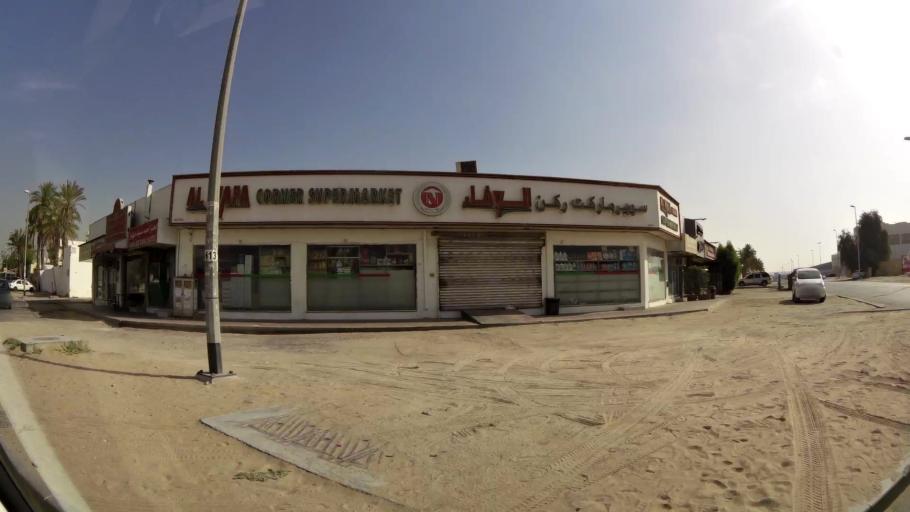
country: AE
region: Ash Shariqah
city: Sharjah
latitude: 25.2583
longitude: 55.4028
